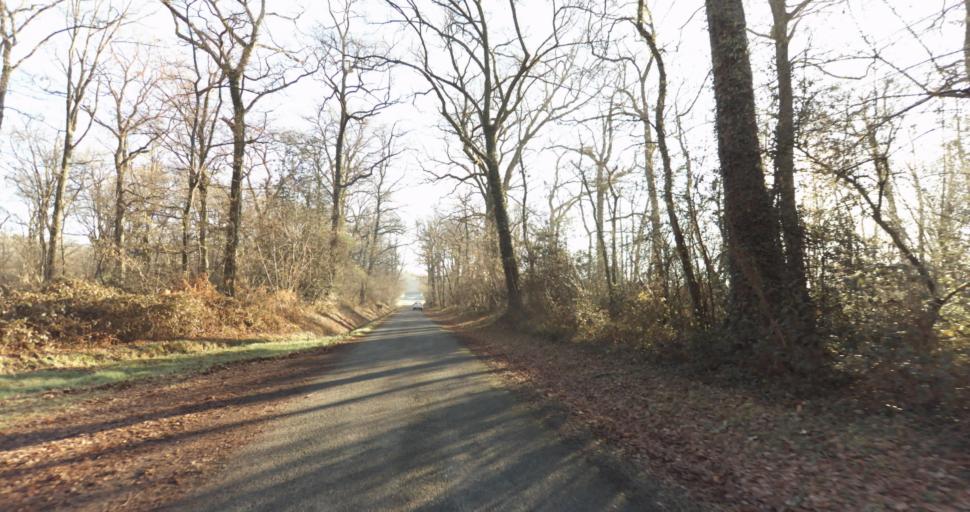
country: FR
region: Aquitaine
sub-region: Departement des Pyrenees-Atlantiques
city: Ousse
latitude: 43.3122
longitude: -0.2517
